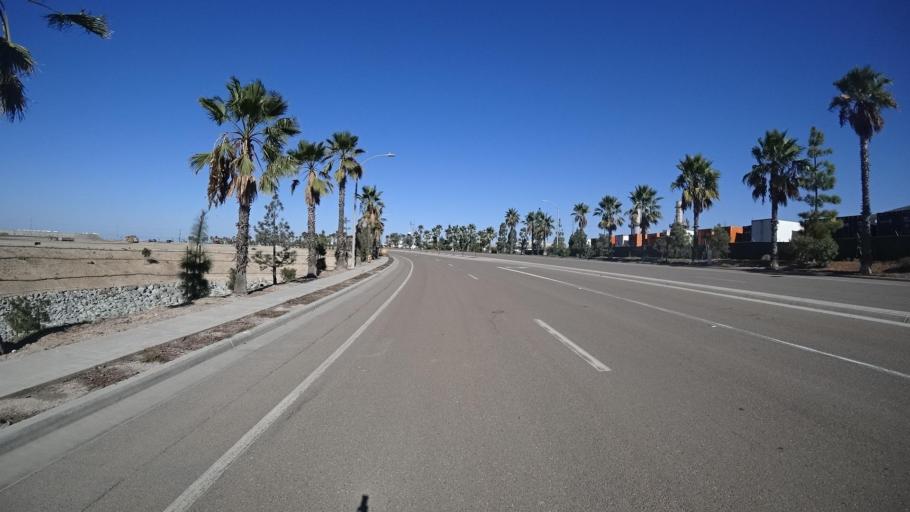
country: MX
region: Baja California
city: Tijuana
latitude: 32.5697
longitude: -116.9136
